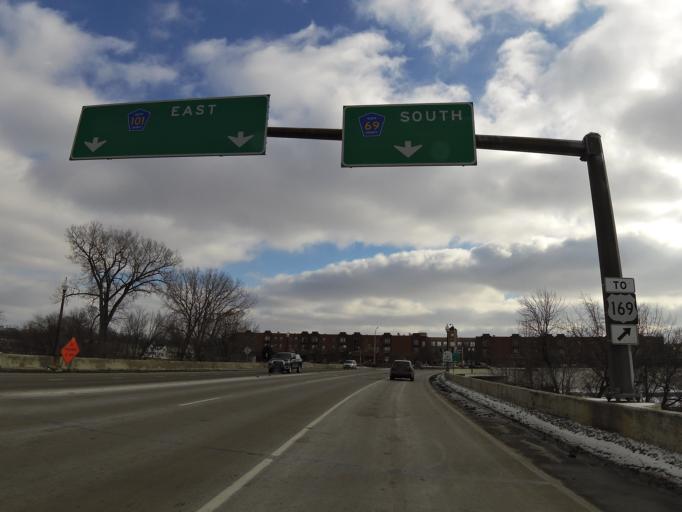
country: US
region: Minnesota
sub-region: Scott County
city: Shakopee
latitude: 44.8007
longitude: -93.5261
